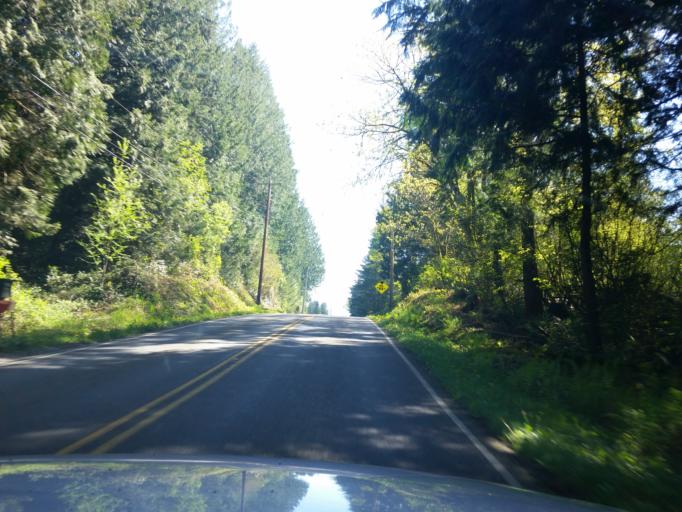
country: US
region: Washington
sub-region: Snohomish County
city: Three Lakes
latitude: 47.9635
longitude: -122.0136
